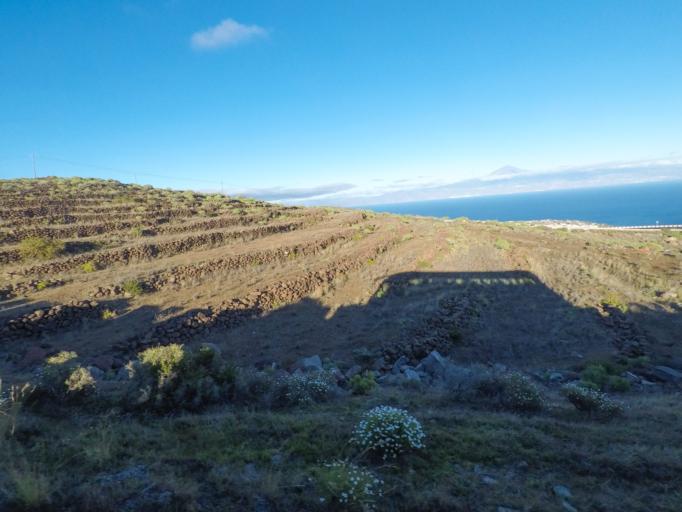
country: ES
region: Canary Islands
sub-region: Provincia de Santa Cruz de Tenerife
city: San Sebastian de la Gomera
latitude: 28.0852
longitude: -17.1447
